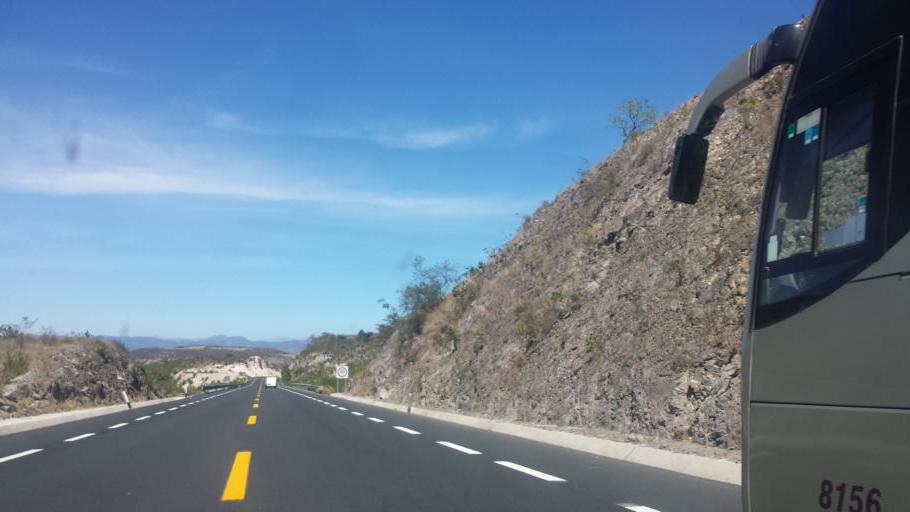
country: MX
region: Oaxaca
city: San Gabriel Casa Blanca
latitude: 17.9564
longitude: -97.3560
